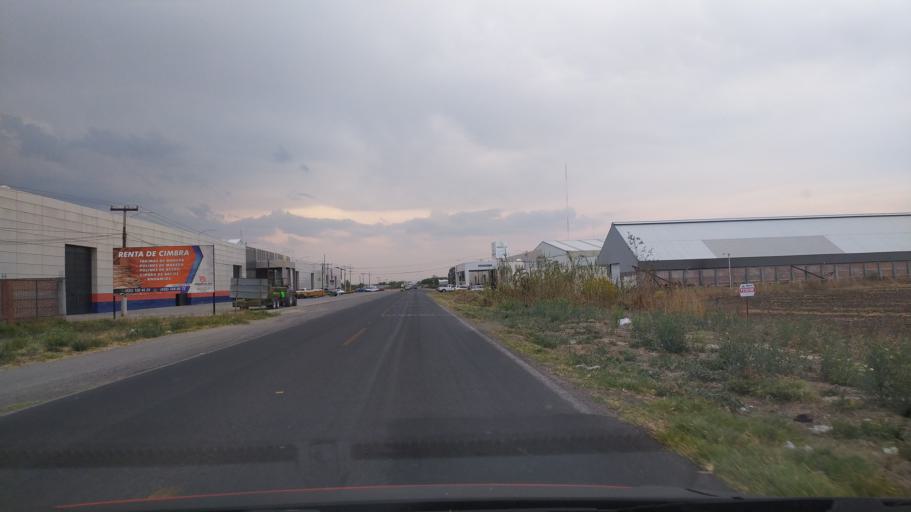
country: MX
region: Guanajuato
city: Ciudad Manuel Doblado
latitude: 20.7449
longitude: -101.9285
